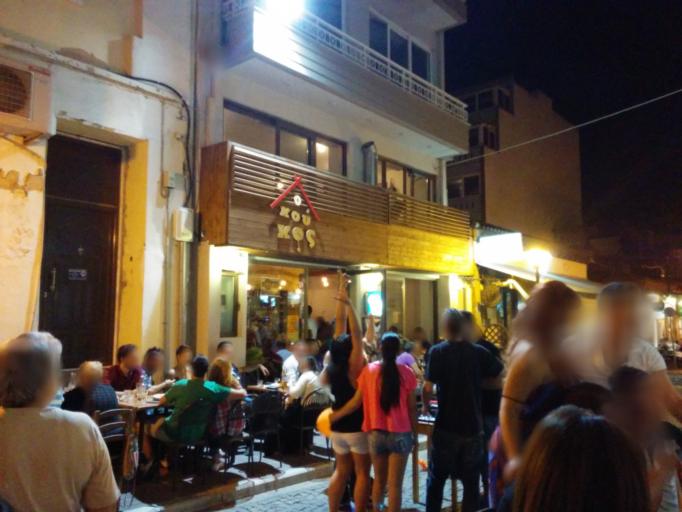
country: GR
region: East Macedonia and Thrace
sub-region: Nomos Evrou
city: Alexandroupoli
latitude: 40.8457
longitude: 25.8767
